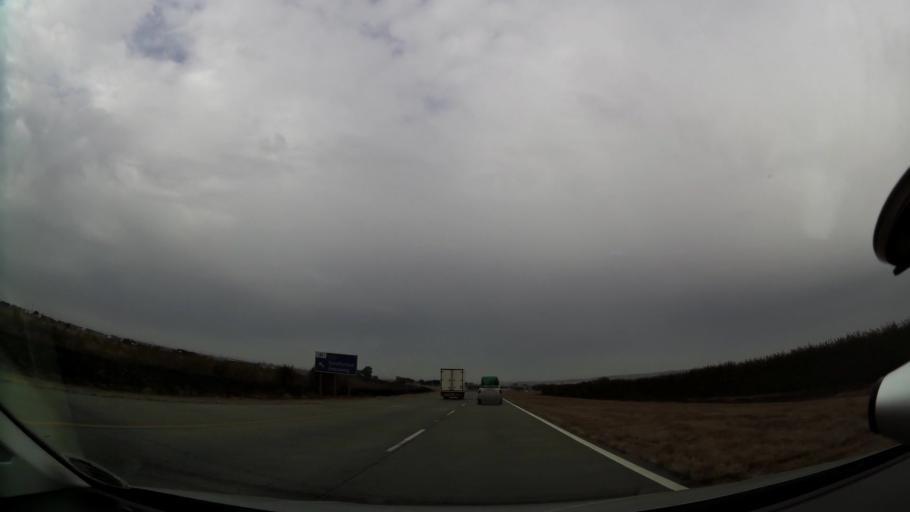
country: ZA
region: Gauteng
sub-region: City of Johannesburg Metropolitan Municipality
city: Orange Farm
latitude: -26.5277
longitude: 27.8092
